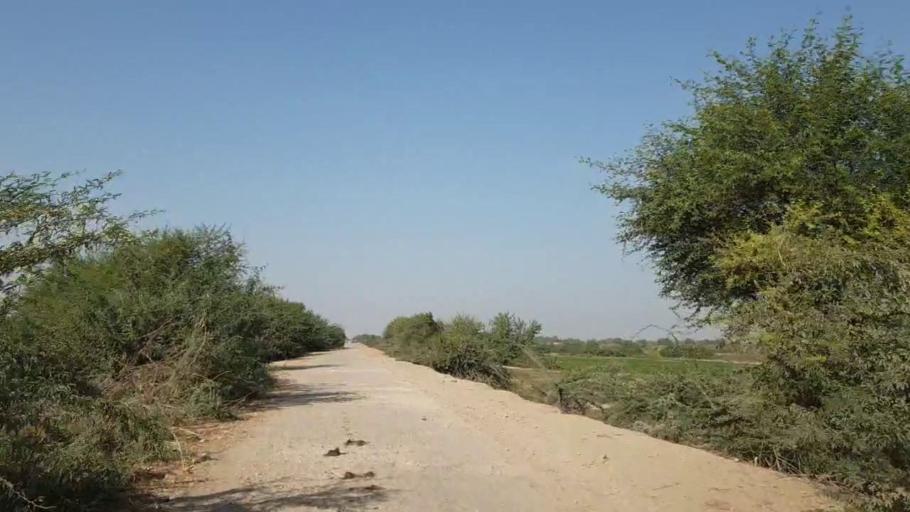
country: PK
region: Sindh
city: Digri
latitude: 24.9855
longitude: 69.1098
